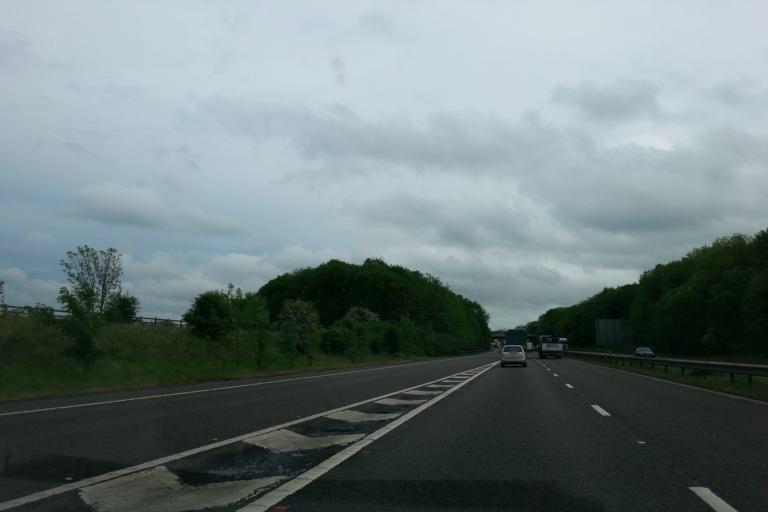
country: GB
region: England
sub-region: Doncaster
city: Stainton
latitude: 53.4760
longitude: -1.1449
